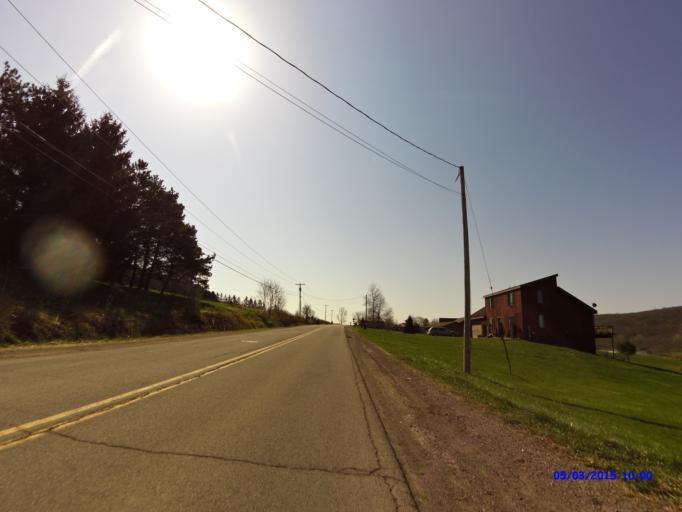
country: US
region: New York
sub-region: Cattaraugus County
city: Franklinville
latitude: 42.3299
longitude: -78.4405
